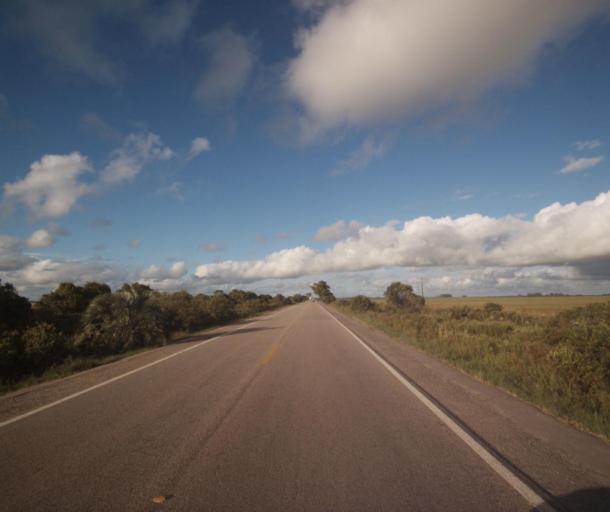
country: BR
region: Rio Grande do Sul
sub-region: Rio Grande
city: Rio Grande
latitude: -32.1801
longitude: -52.4224
